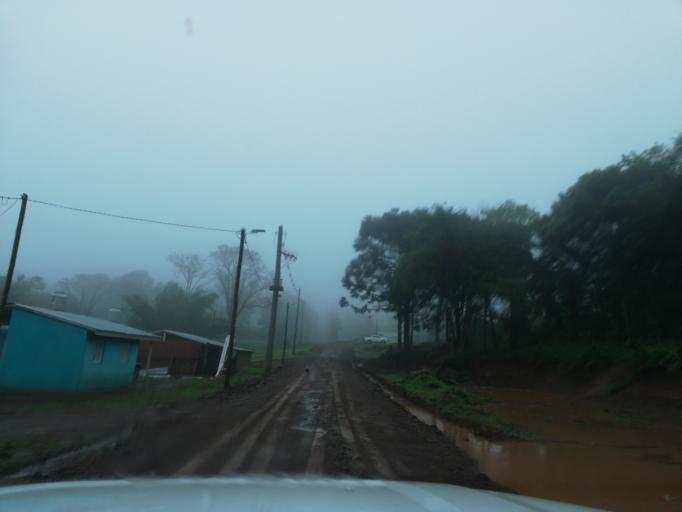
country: AR
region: Misiones
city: Almafuerte
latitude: -27.5120
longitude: -55.4014
